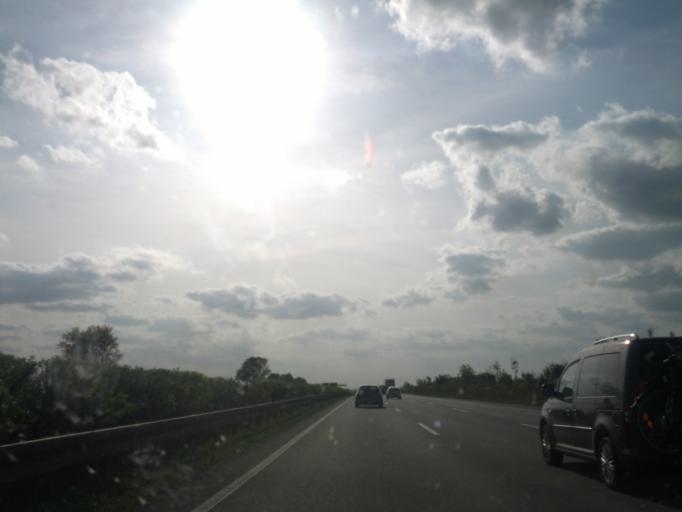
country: DE
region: Thuringia
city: Neudietendorf
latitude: 50.8936
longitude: 10.9196
